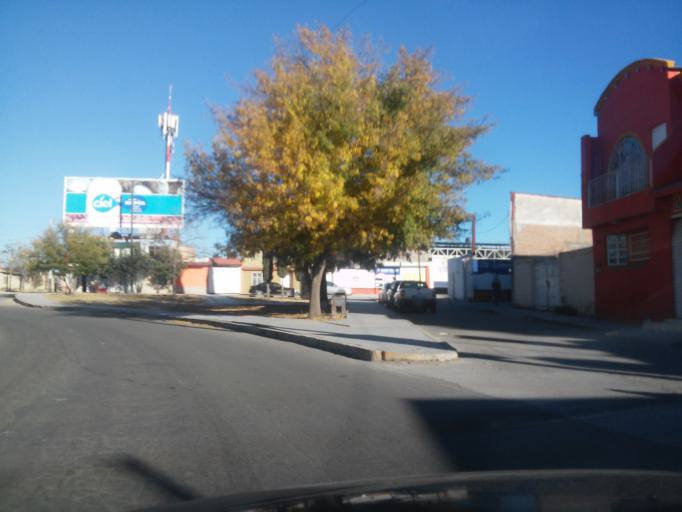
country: MX
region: Durango
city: Victoria de Durango
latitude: 24.0155
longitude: -104.6386
